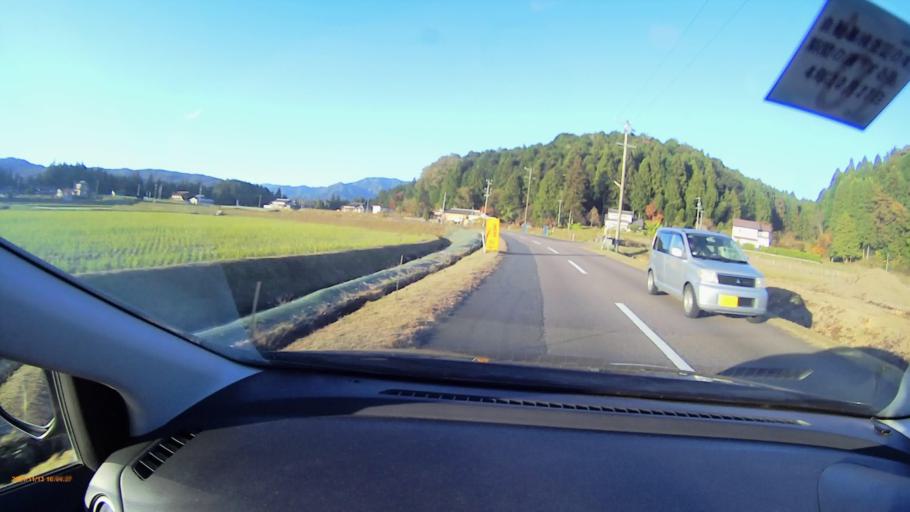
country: JP
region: Gifu
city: Nakatsugawa
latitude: 35.5929
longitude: 137.4707
